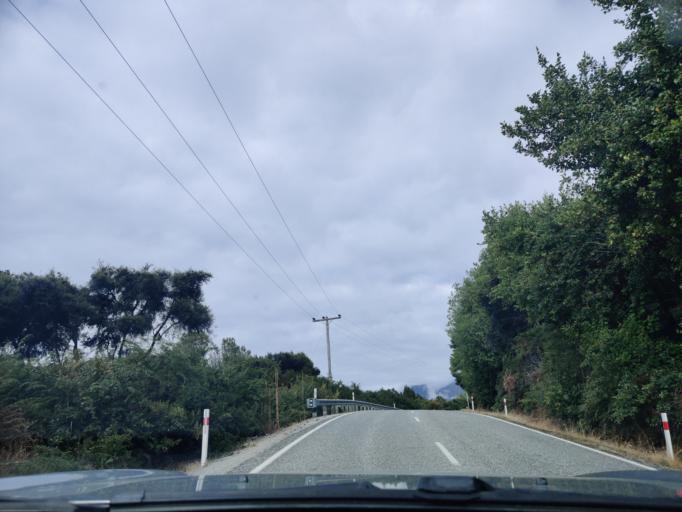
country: NZ
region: Otago
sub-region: Queenstown-Lakes District
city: Queenstown
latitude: -45.0746
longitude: 168.4950
